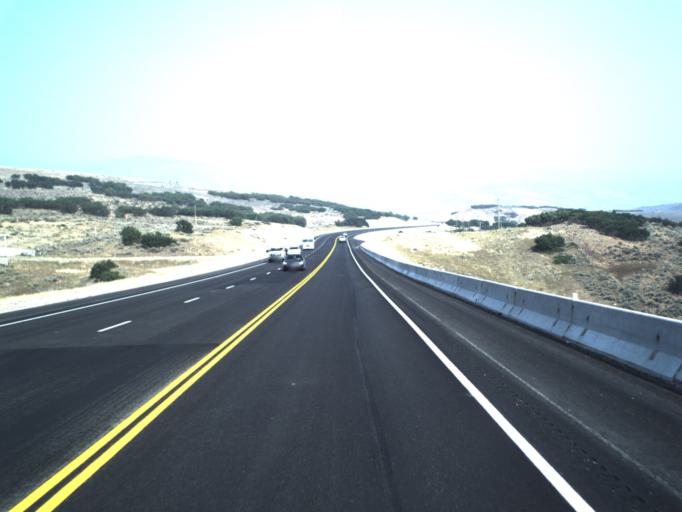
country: US
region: Utah
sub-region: Summit County
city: Kamas
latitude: 40.6346
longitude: -111.3628
